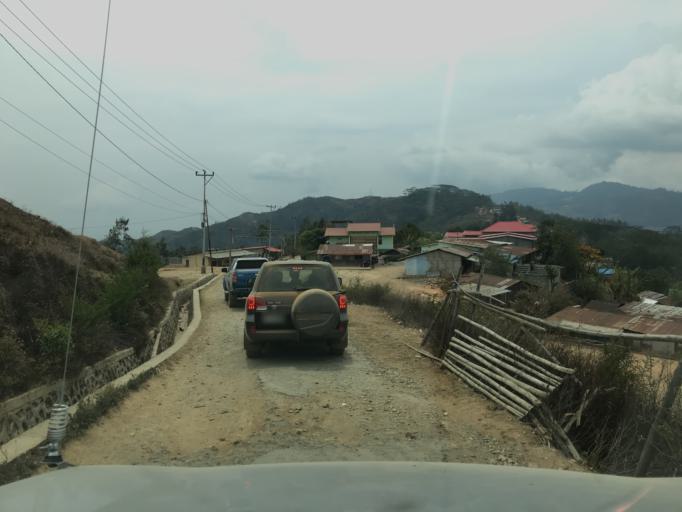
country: TL
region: Ermera
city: Gleno
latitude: -8.8372
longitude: 125.4313
